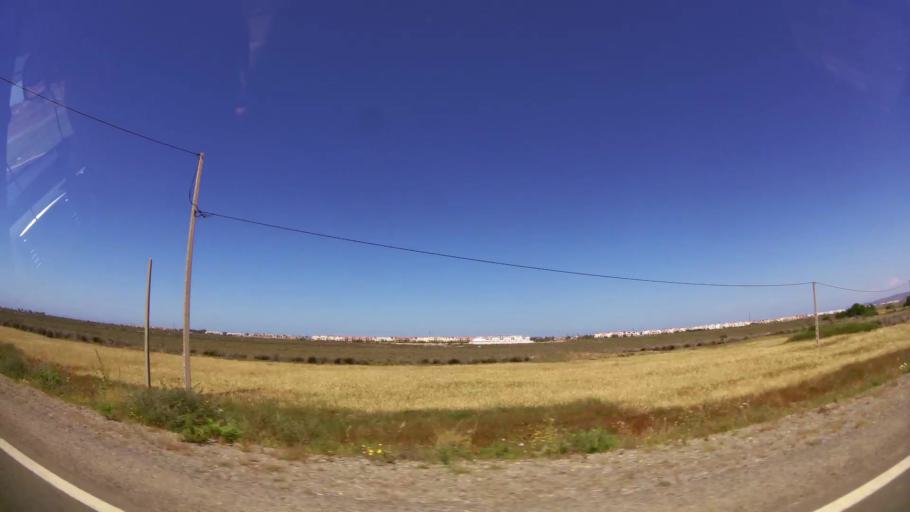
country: MA
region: Oriental
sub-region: Berkane-Taourirt
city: Madagh
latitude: 35.0967
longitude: -2.3187
